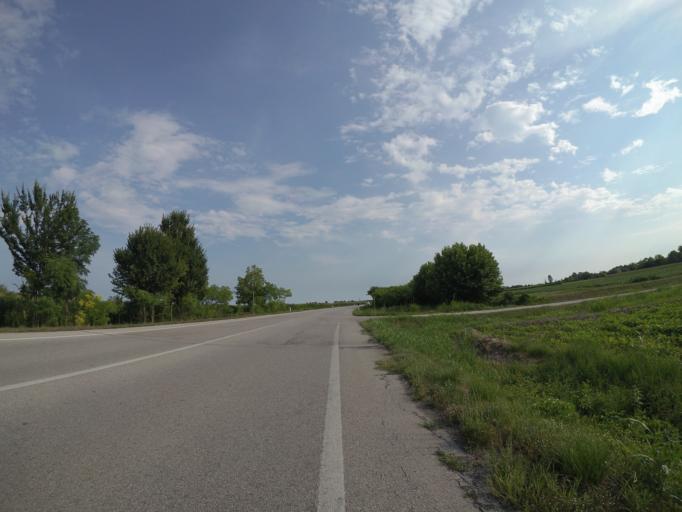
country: IT
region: Friuli Venezia Giulia
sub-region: Provincia di Udine
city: Codroipo
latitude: 45.9433
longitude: 12.9785
